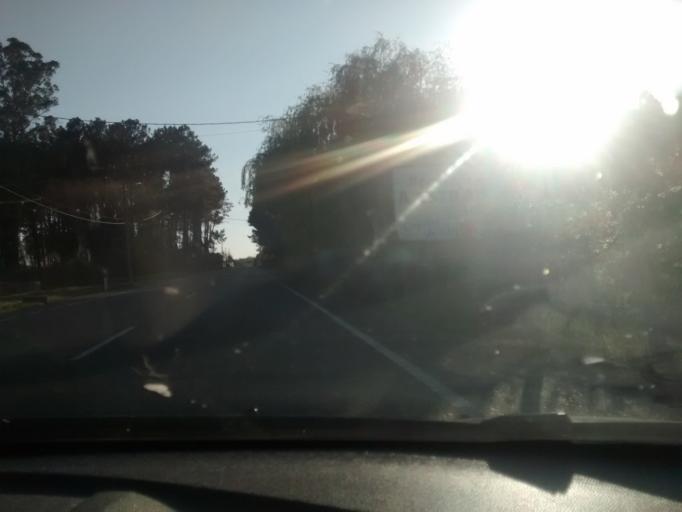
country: ES
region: Galicia
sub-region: Provincia de Pontevedra
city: A Estrada
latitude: 42.6967
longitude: -8.4611
